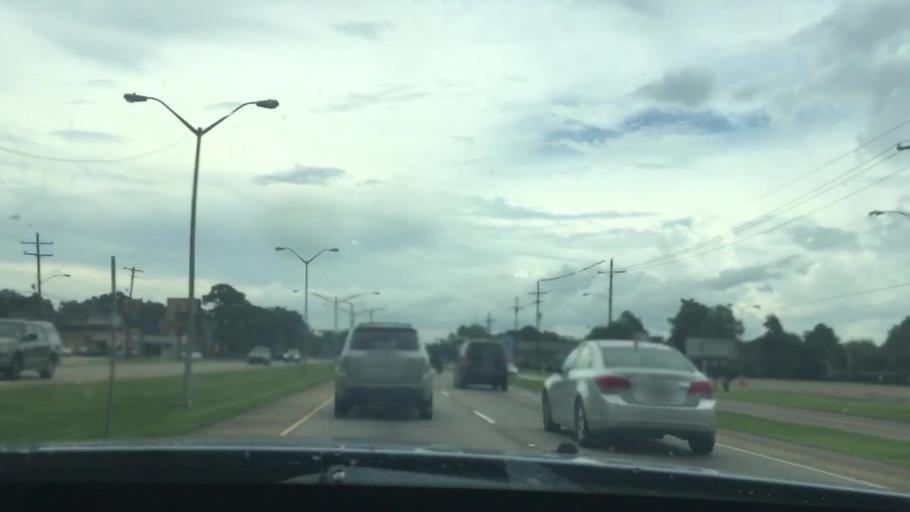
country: US
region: Louisiana
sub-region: East Baton Rouge Parish
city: Westminster
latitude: 30.4544
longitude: -91.0857
